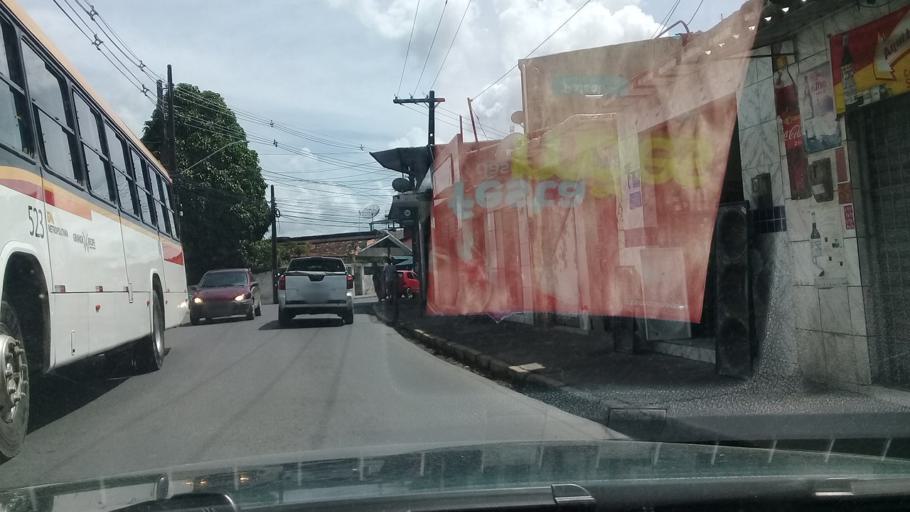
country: BR
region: Pernambuco
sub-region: Jaboatao Dos Guararapes
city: Jaboatao dos Guararapes
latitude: -8.1088
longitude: -35.0162
